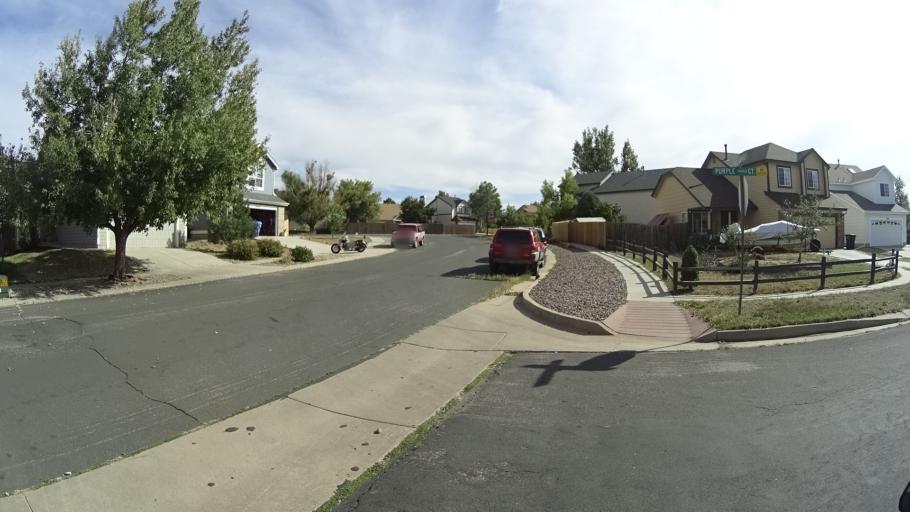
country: US
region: Colorado
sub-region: El Paso County
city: Cimarron Hills
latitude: 38.9057
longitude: -104.6939
